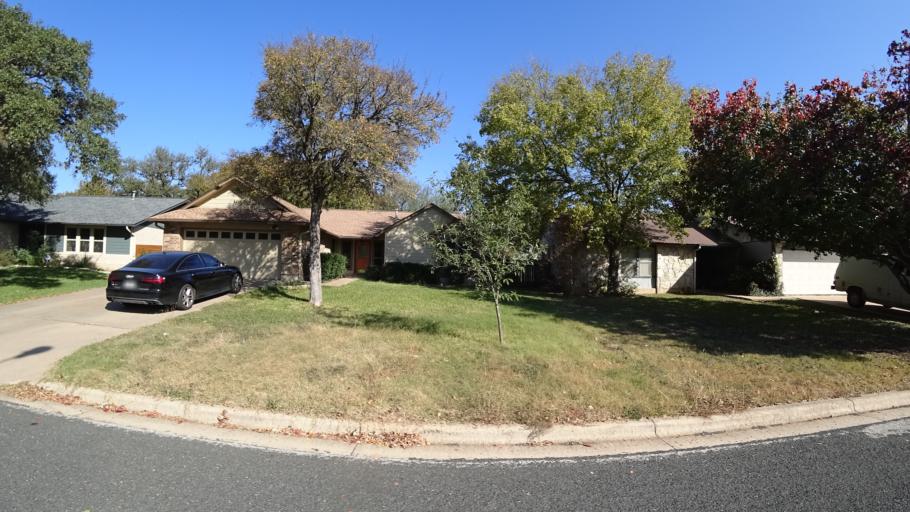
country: US
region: Texas
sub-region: Travis County
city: Barton Creek
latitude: 30.2313
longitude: -97.8517
